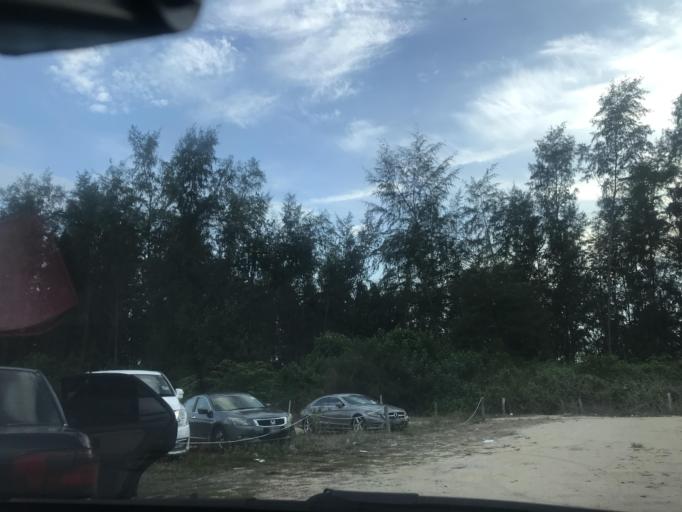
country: MY
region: Kelantan
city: Peringat
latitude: 6.1306
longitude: 102.3691
